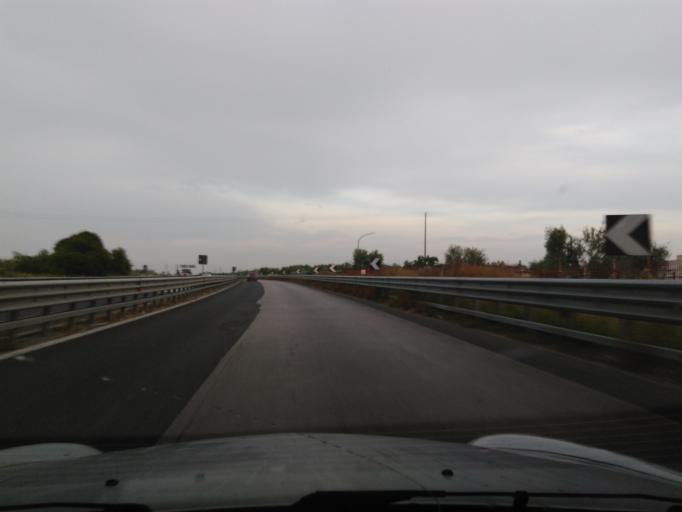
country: IT
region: Apulia
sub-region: Provincia di Bari
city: Giovinazzo
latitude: 41.1750
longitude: 16.6579
